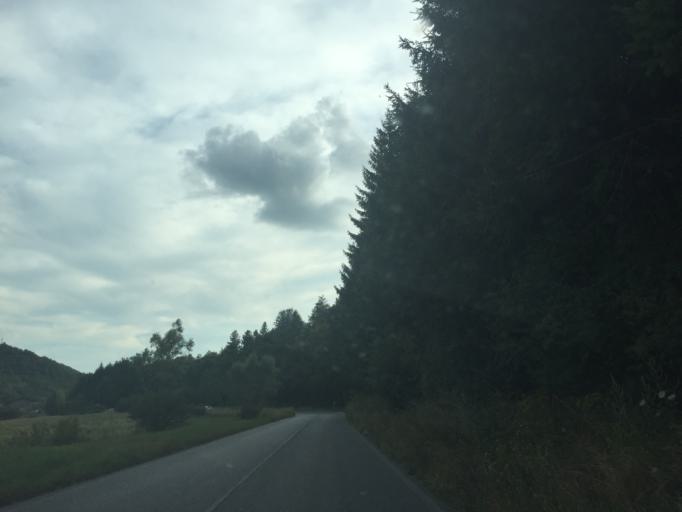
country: IT
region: Tuscany
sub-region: Provincia di Pistoia
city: Campo Tizzoro
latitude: 44.0319
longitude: 10.8739
